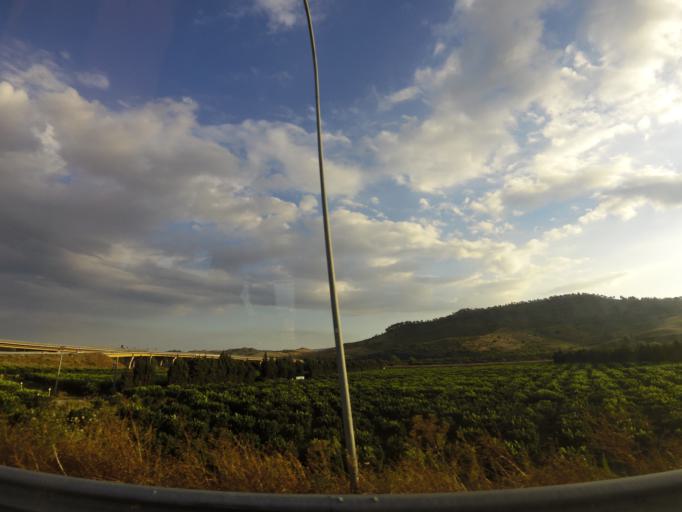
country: IT
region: Calabria
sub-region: Provincia di Catanzaro
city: Catanzaro
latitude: 38.8537
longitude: 16.5750
